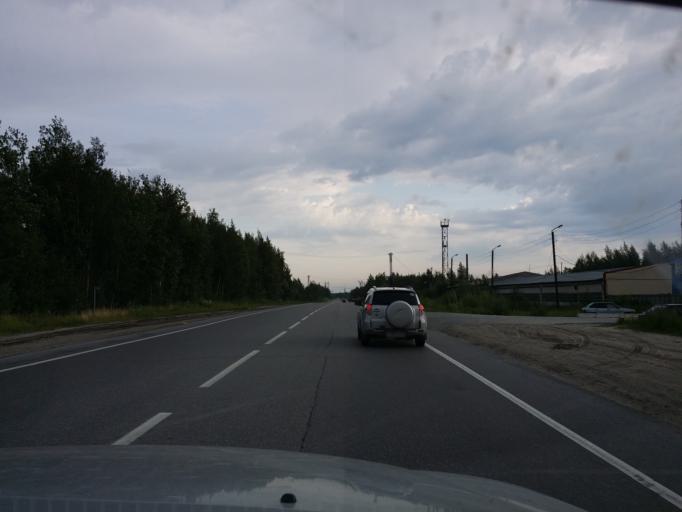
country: RU
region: Khanty-Mansiyskiy Avtonomnyy Okrug
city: Megion
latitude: 61.0717
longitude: 76.1162
